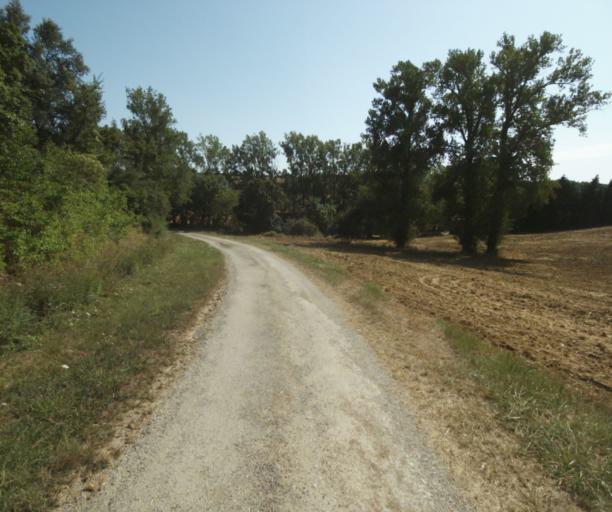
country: FR
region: Midi-Pyrenees
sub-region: Departement de la Haute-Garonne
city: Saint-Felix-Lauragais
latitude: 43.4375
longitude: 1.8473
